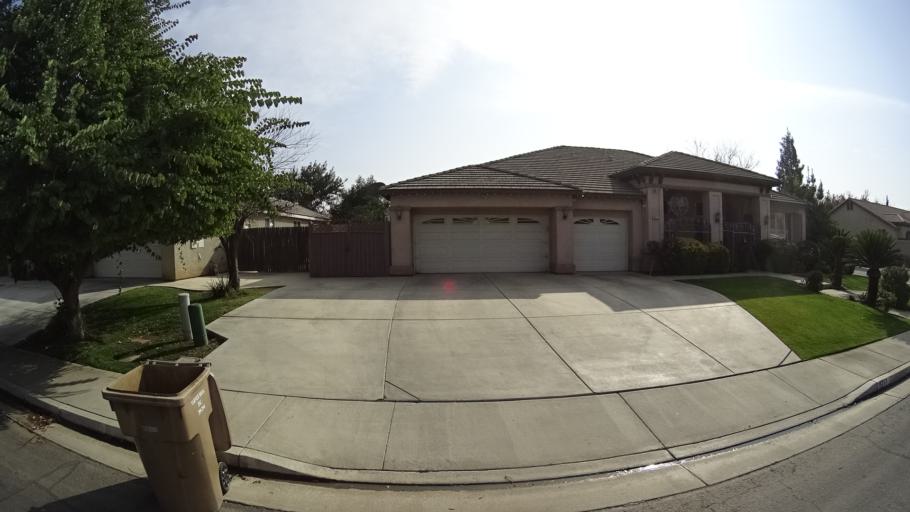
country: US
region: California
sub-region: Kern County
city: Greenacres
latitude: 35.4140
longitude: -119.1054
